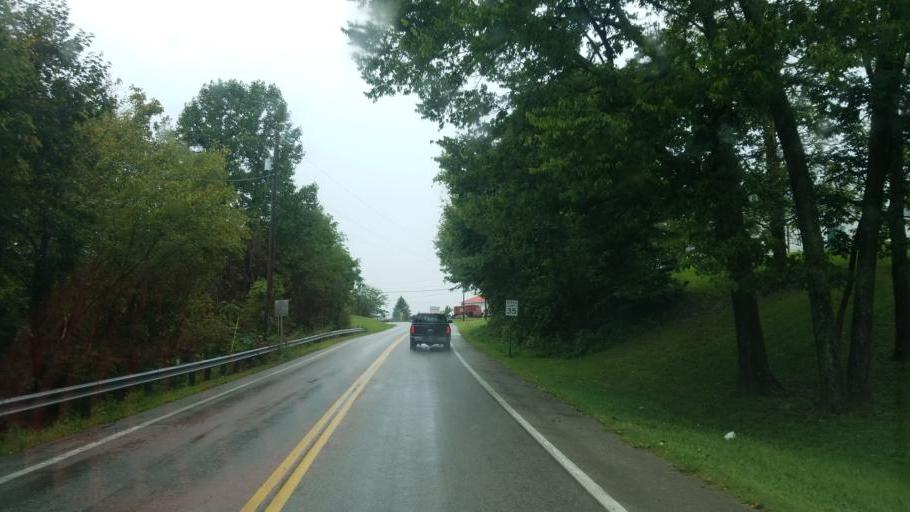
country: US
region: Ohio
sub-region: Adams County
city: West Union
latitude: 38.7967
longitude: -83.5261
